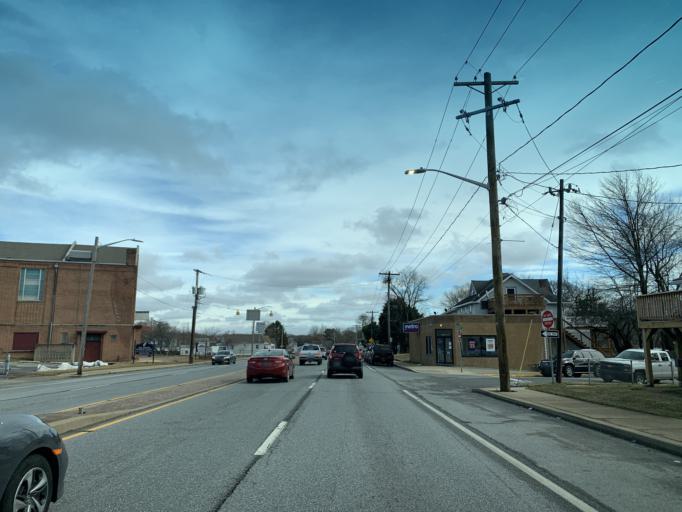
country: US
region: Delaware
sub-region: New Castle County
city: Elsmere
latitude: 39.7392
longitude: -75.5973
